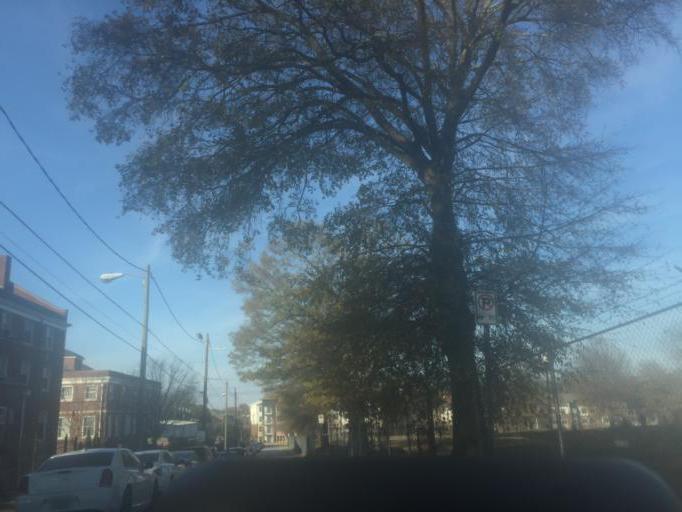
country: US
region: Georgia
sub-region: Fulton County
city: Atlanta
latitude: 33.7476
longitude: -84.4111
